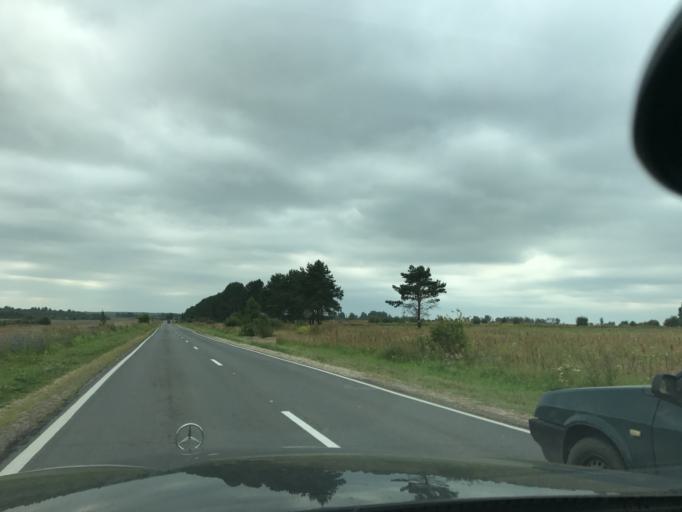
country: RU
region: Vladimir
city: Galitsy
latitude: 56.1701
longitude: 42.8097
